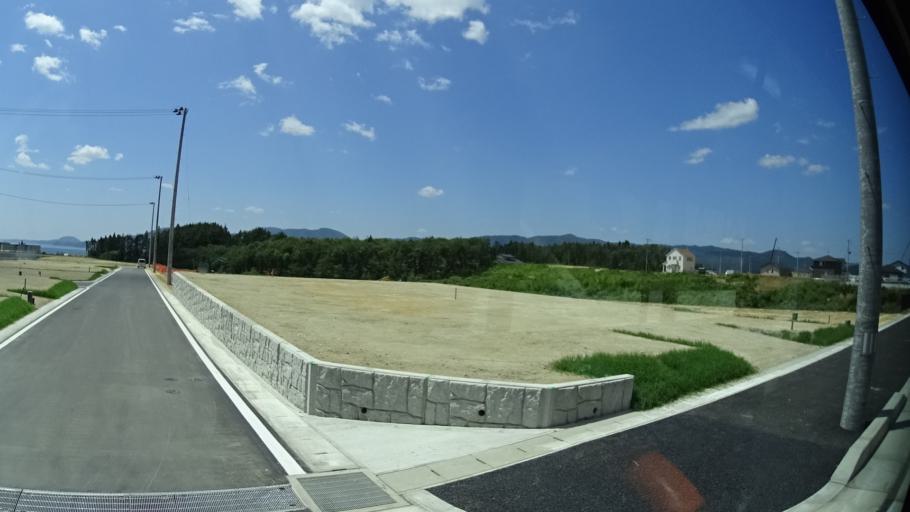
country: JP
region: Iwate
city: Ofunato
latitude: 39.0244
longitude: 141.6448
